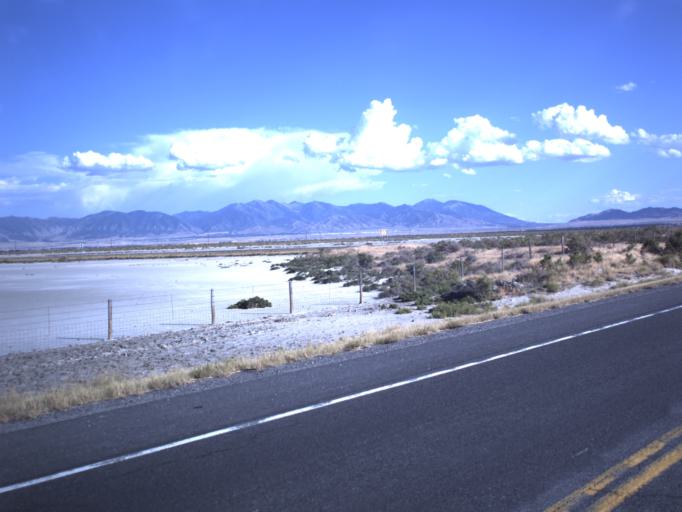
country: US
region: Utah
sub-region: Tooele County
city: Grantsville
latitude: 40.7064
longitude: -112.5302
